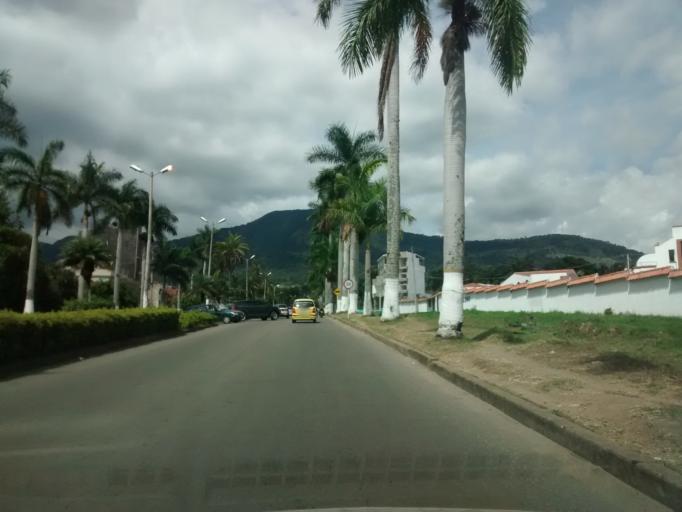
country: CO
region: Cundinamarca
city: Fusagasuga
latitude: 4.3434
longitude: -74.3747
